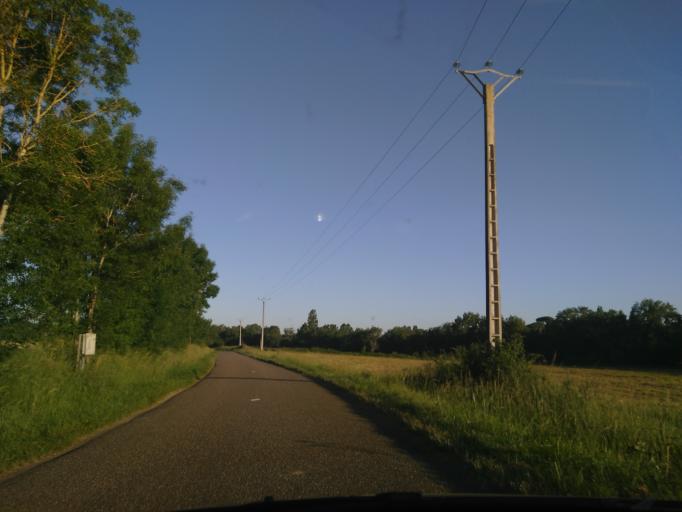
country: FR
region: Midi-Pyrenees
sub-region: Departement du Gers
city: Valence-sur-Baise
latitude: 43.8695
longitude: 0.4446
